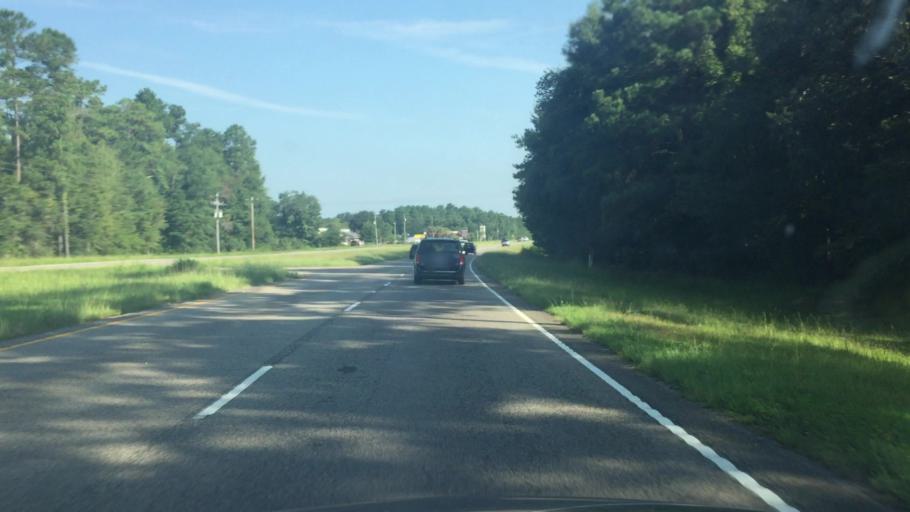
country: US
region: South Carolina
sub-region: Horry County
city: North Myrtle Beach
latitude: 33.9209
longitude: -78.7247
